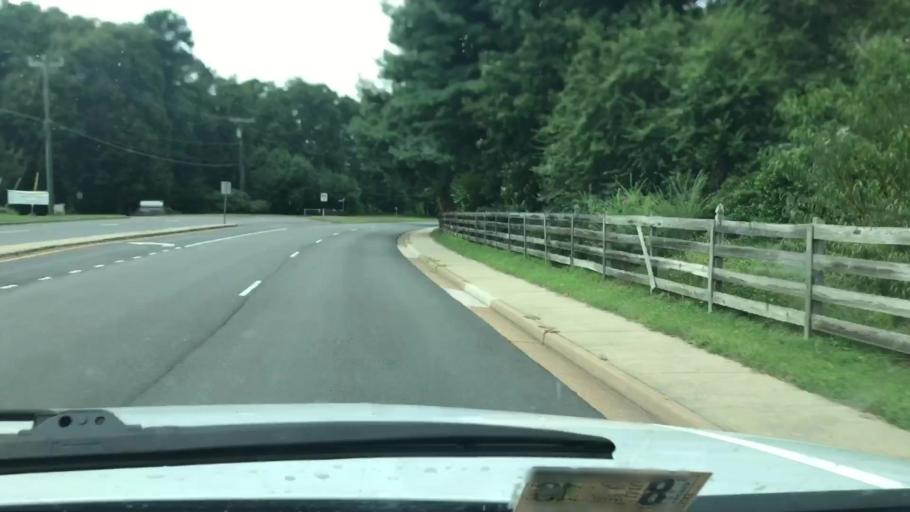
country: US
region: Virginia
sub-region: Henrico County
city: Short Pump
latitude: 37.6252
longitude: -77.6085
